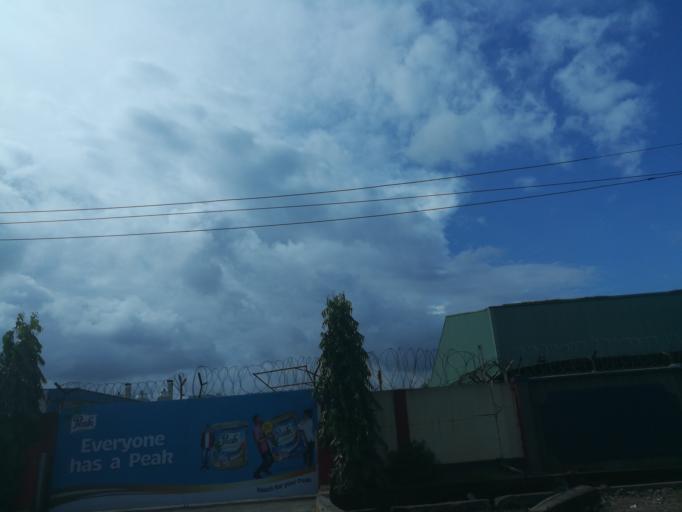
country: NG
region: Lagos
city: Agege
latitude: 6.6237
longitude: 3.3405
